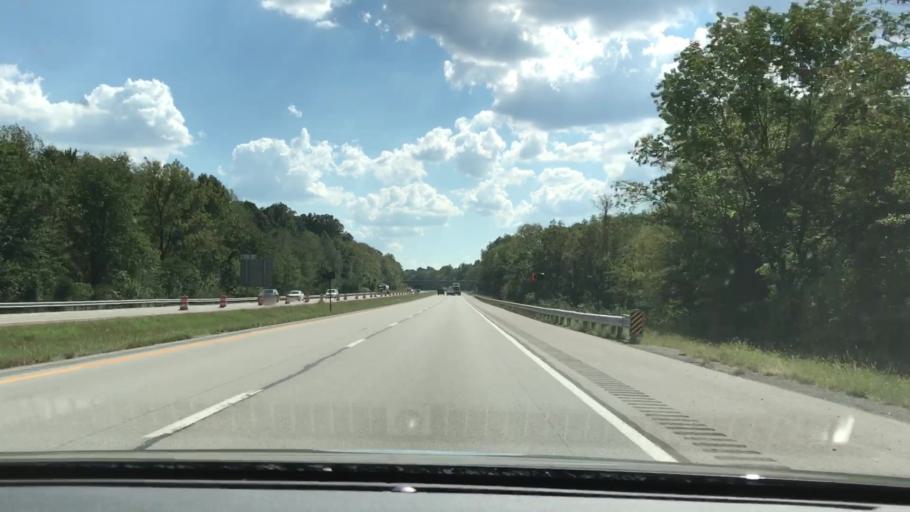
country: US
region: Kentucky
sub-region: Ohio County
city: Oak Grove
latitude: 37.2725
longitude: -86.7467
